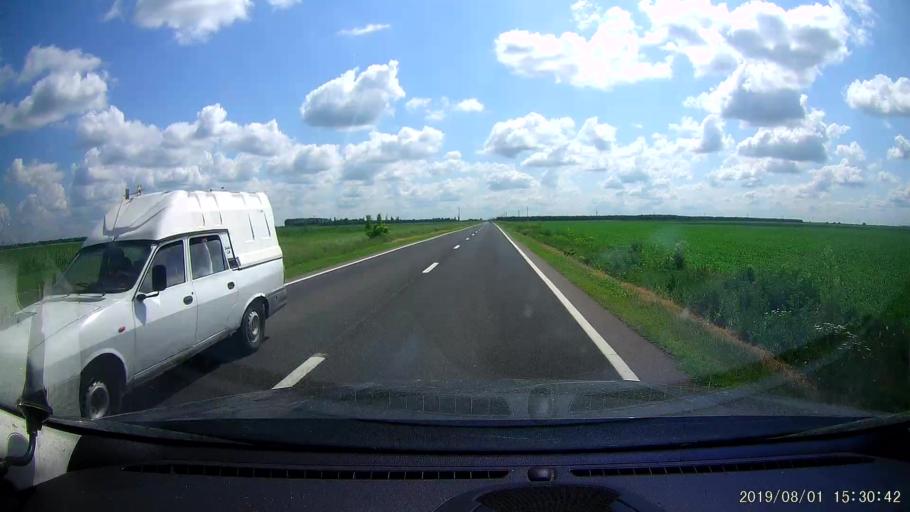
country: RO
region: Braila
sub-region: Comuna Viziru
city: Viziru
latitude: 44.9588
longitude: 27.6726
